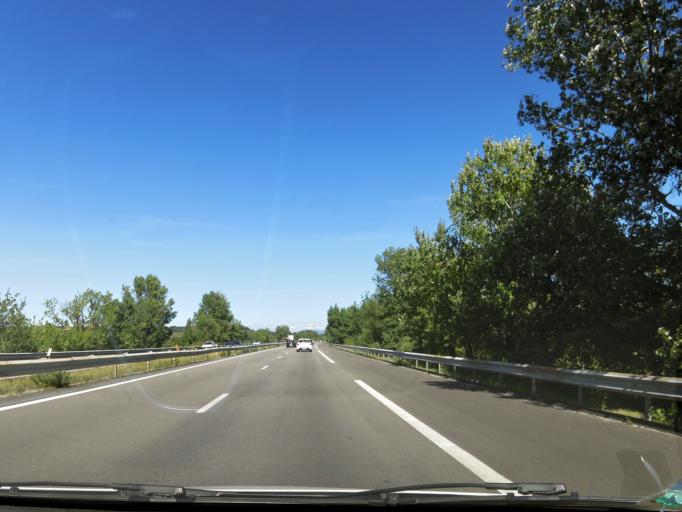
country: FR
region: Languedoc-Roussillon
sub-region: Departement du Gard
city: Pujaut
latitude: 44.0277
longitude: 4.7458
